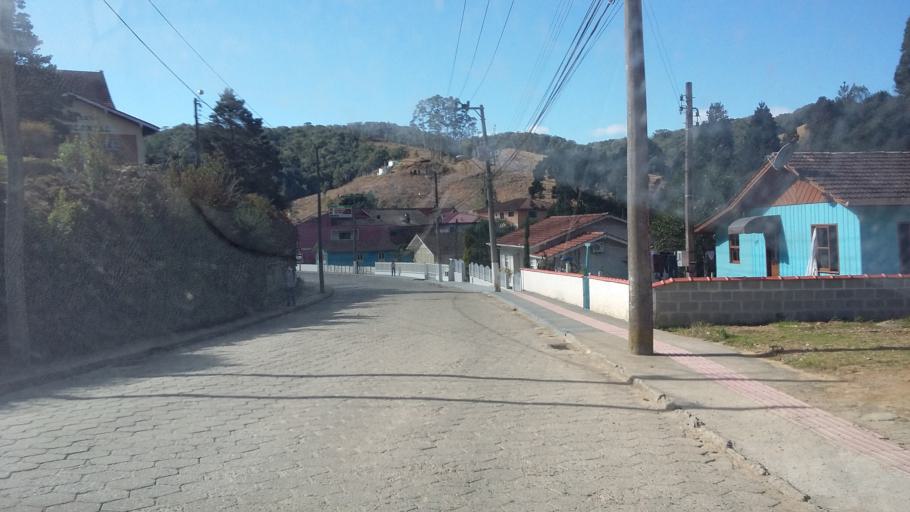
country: BR
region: Santa Catarina
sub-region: Santo Amaro Da Imperatriz
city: Santo Amaro da Imperatriz
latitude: -27.6741
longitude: -49.0147
